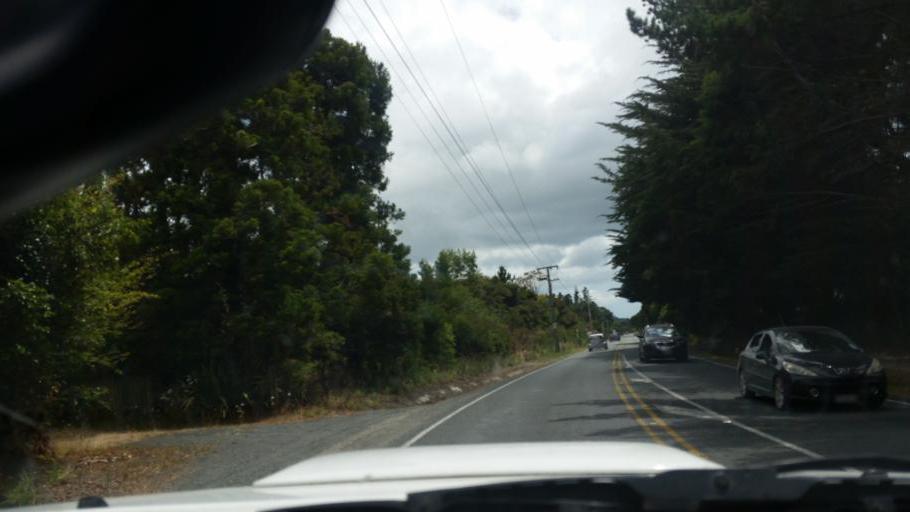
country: NZ
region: Auckland
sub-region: Auckland
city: Wellsford
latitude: -36.1219
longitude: 174.5719
